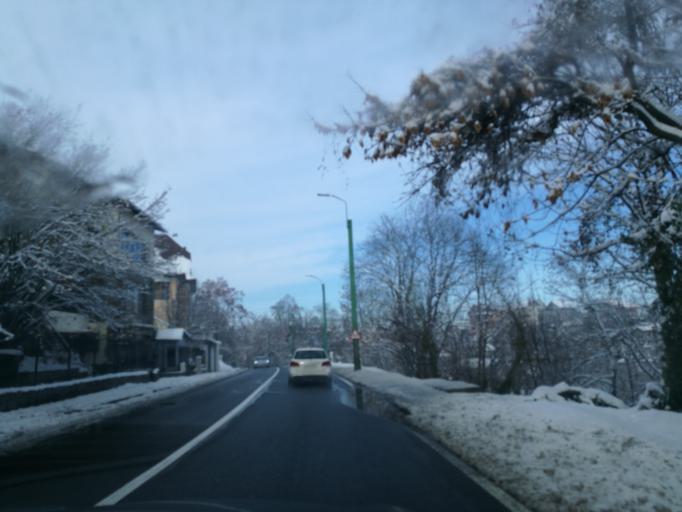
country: RO
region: Brasov
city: Brasov
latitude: 45.6457
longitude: 25.5851
